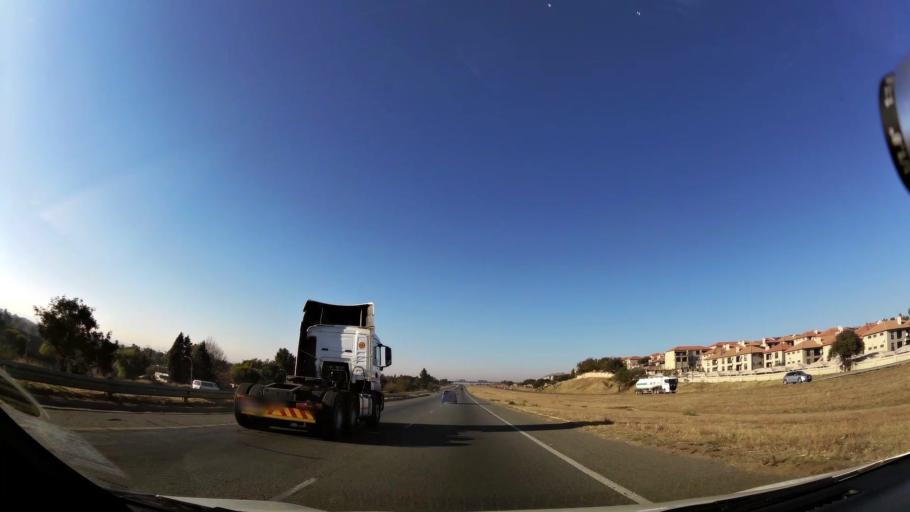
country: ZA
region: Gauteng
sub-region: Ekurhuleni Metropolitan Municipality
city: Germiston
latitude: -26.2885
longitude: 28.1027
